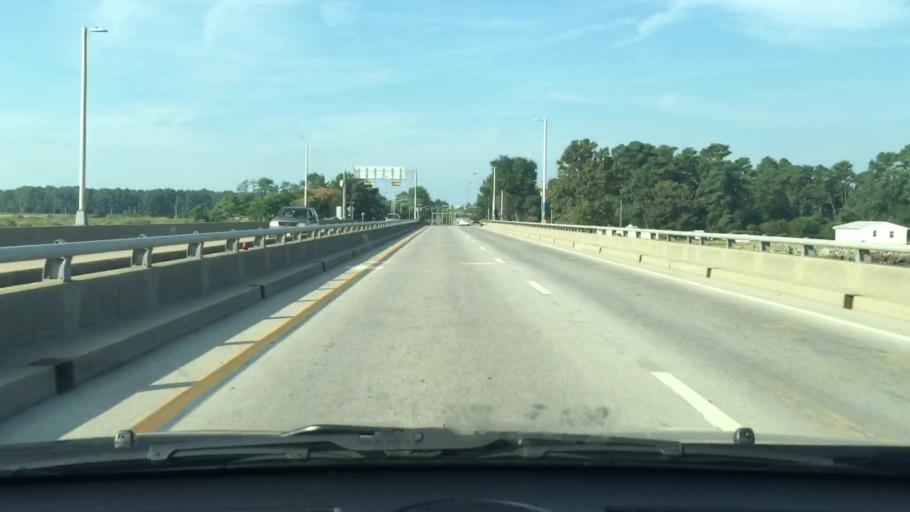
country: US
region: Virginia
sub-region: Isle of Wight County
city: Carrollton
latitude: 36.9727
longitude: -76.5058
